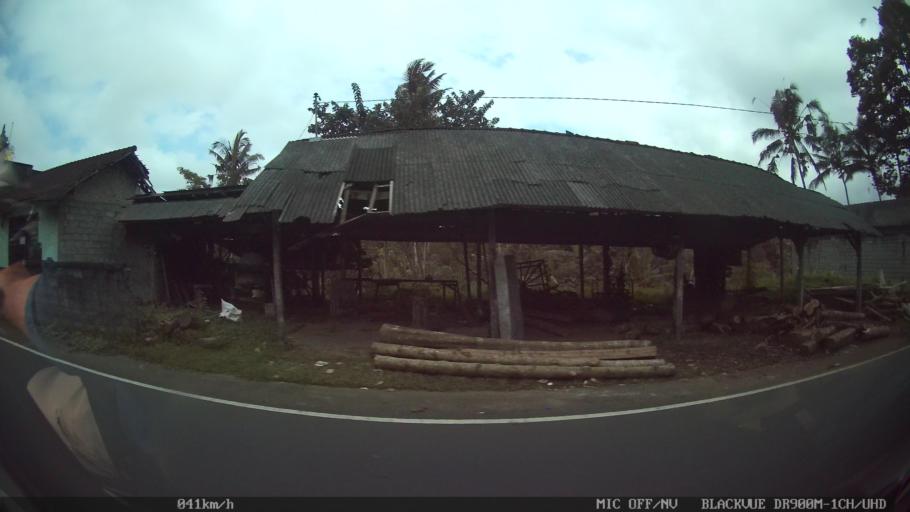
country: ID
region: Bali
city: Banjar Brahmanabukit
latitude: -8.4493
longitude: 115.3795
